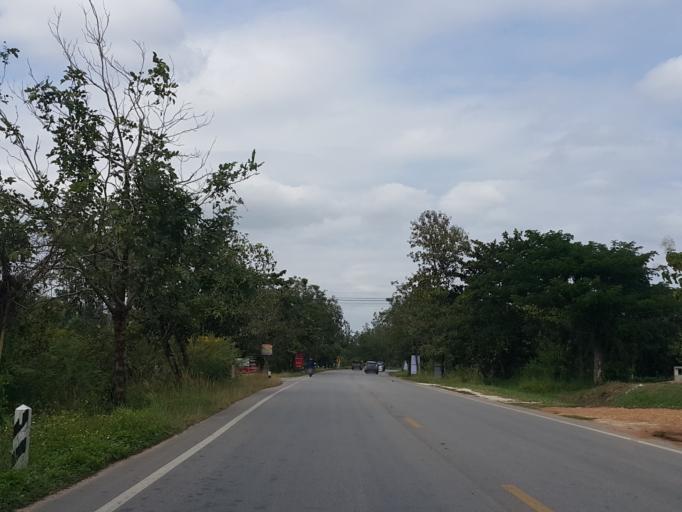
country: TH
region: Lampang
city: Lampang
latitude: 18.3310
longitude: 99.4628
